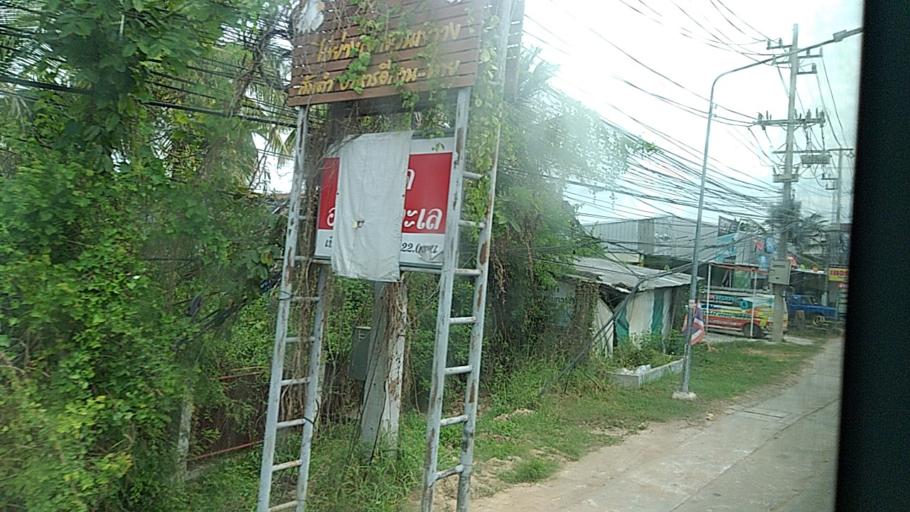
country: TH
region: Maha Sarakham
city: Maha Sarakham
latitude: 16.1772
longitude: 103.3134
